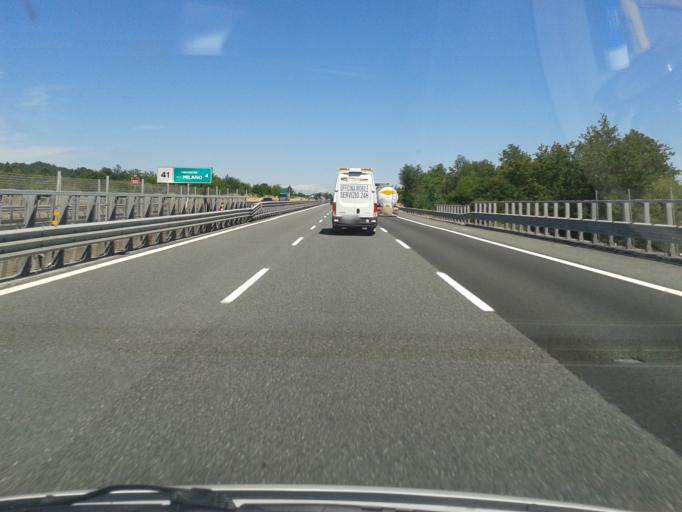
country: IT
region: Piedmont
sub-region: Provincia di Alessandria
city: Capriata d'Orba
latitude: 44.7261
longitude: 8.6662
